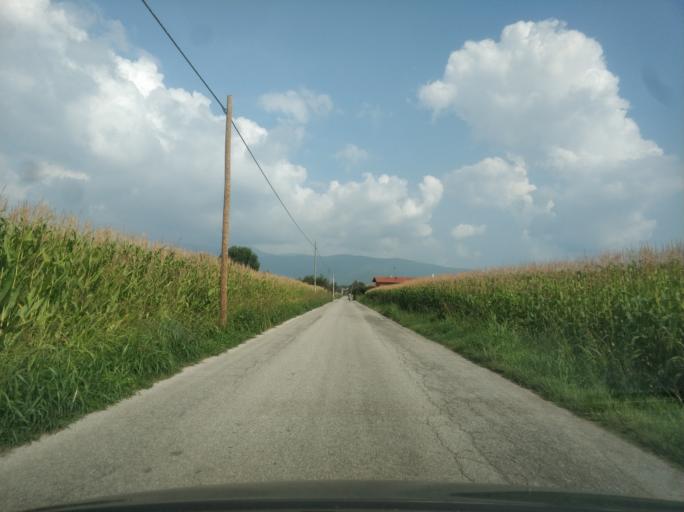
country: IT
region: Piedmont
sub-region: Provincia di Cuneo
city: Caraglio
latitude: 44.4307
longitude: 7.4335
